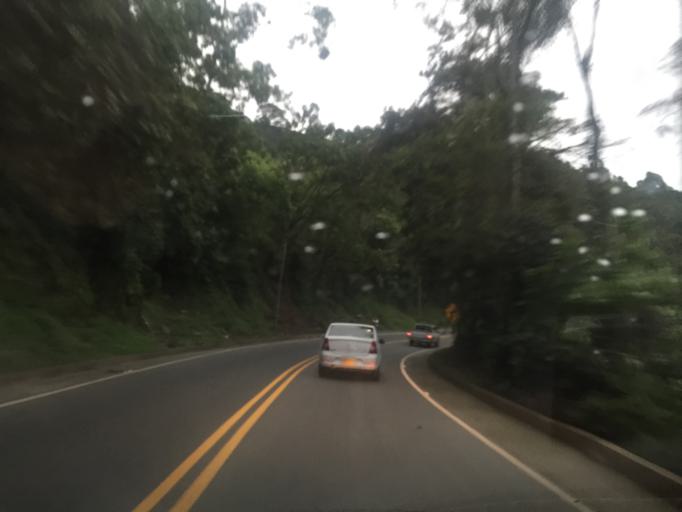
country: CO
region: Caldas
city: Chinchina
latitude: 5.0110
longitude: -75.5584
